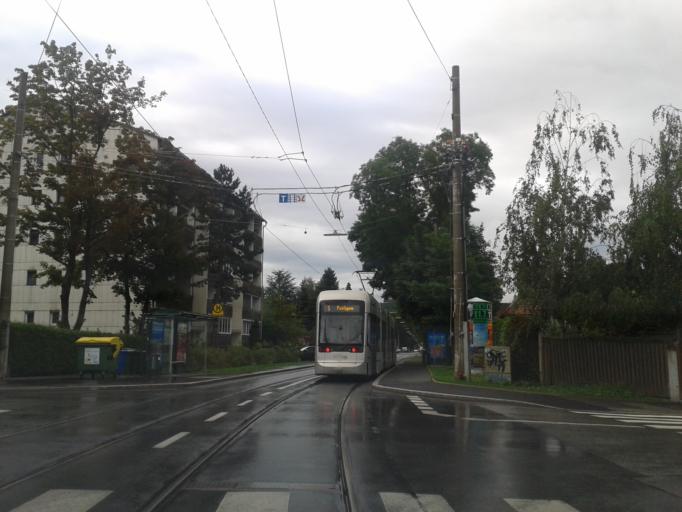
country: AT
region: Styria
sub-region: Graz Stadt
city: Goesting
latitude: 47.0907
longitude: 15.4272
